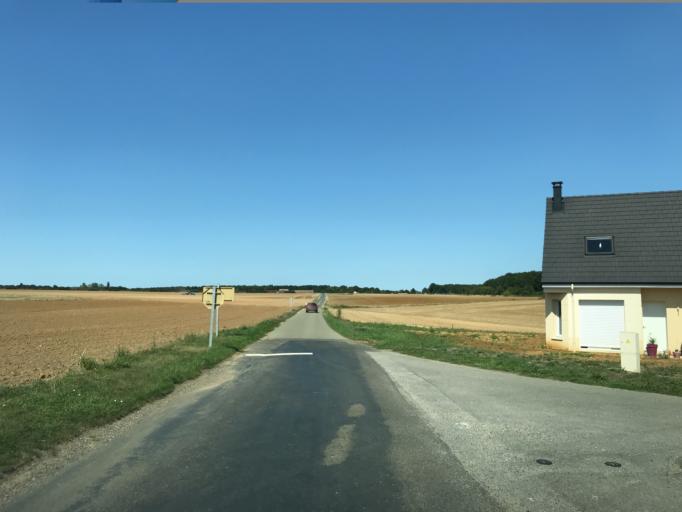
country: FR
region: Haute-Normandie
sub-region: Departement de l'Eure
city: Houlbec-Cocherel
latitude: 49.0648
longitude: 1.2687
